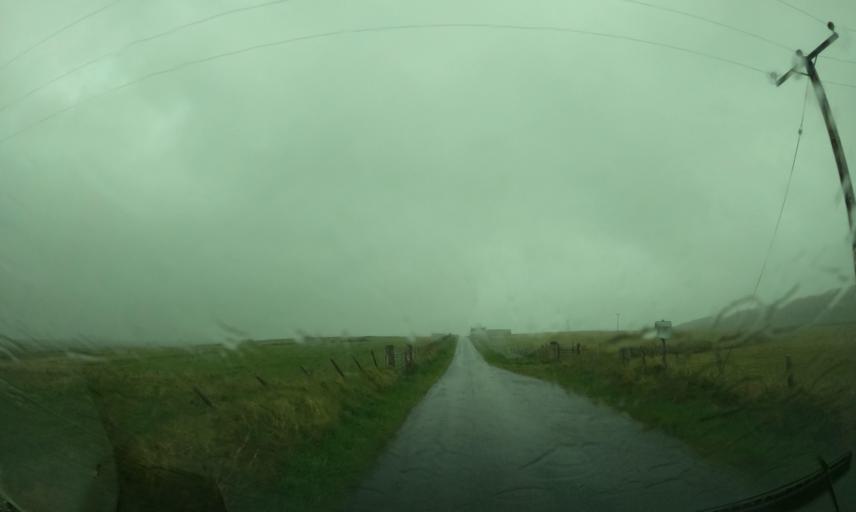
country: GB
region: Scotland
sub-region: Eilean Siar
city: Barra
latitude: 56.4601
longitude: -6.9335
